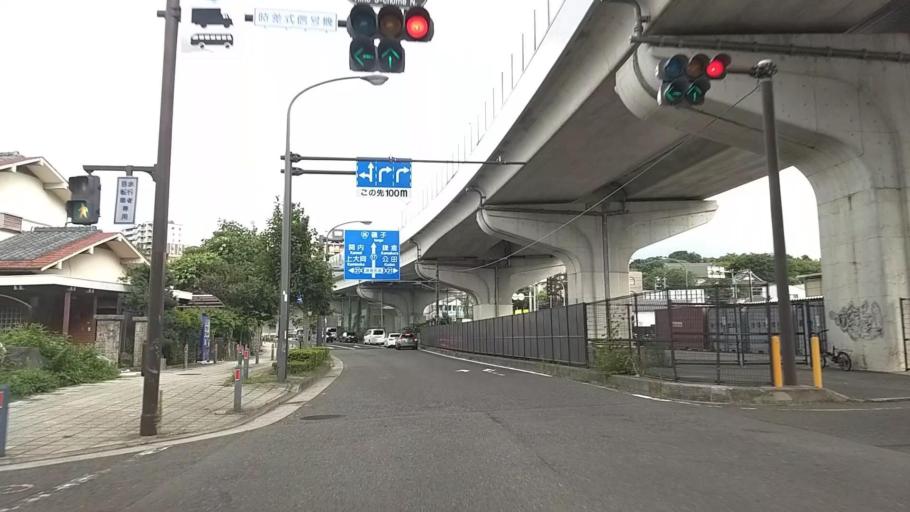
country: JP
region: Kanagawa
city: Yokohama
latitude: 35.3949
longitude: 139.5839
